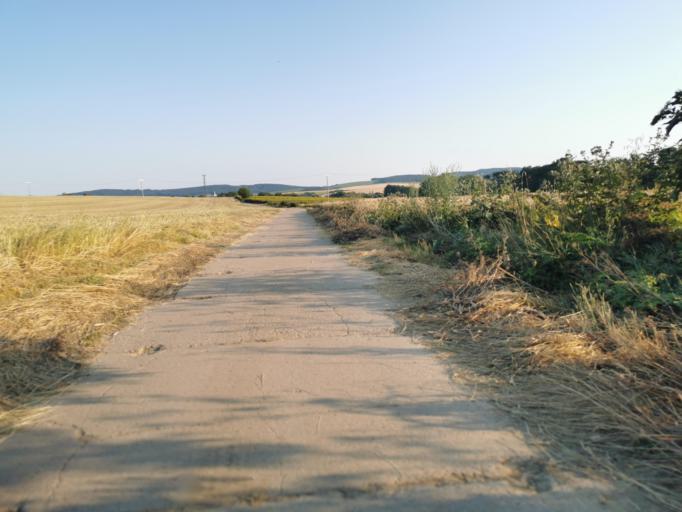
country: SK
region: Trnavsky
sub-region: Okres Skalica
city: Skalica
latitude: 48.7834
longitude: 17.2789
